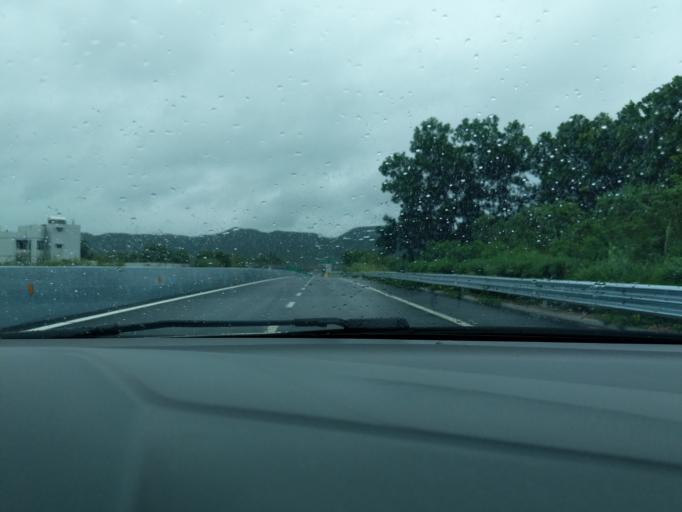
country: CN
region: Guangdong
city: Pingshi
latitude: 22.2394
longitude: 112.3051
